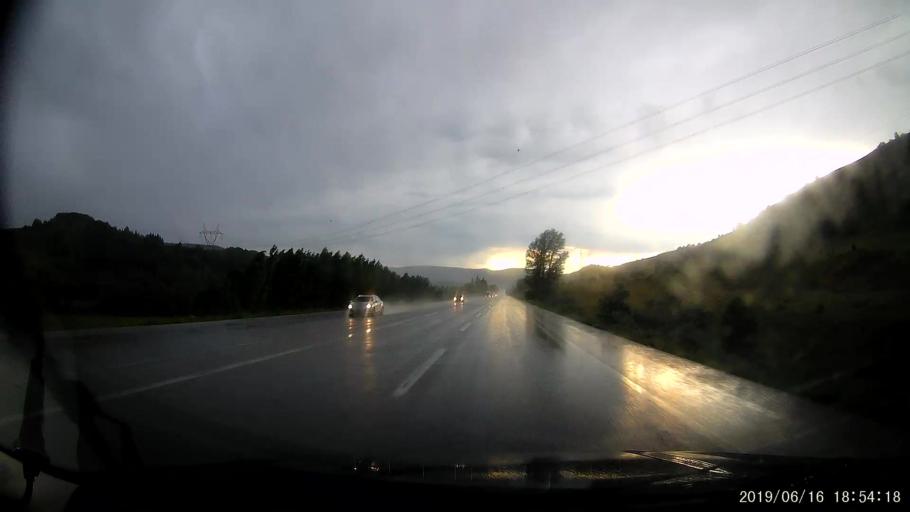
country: TR
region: Erzincan
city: Catalcam
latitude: 39.8965
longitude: 38.8570
